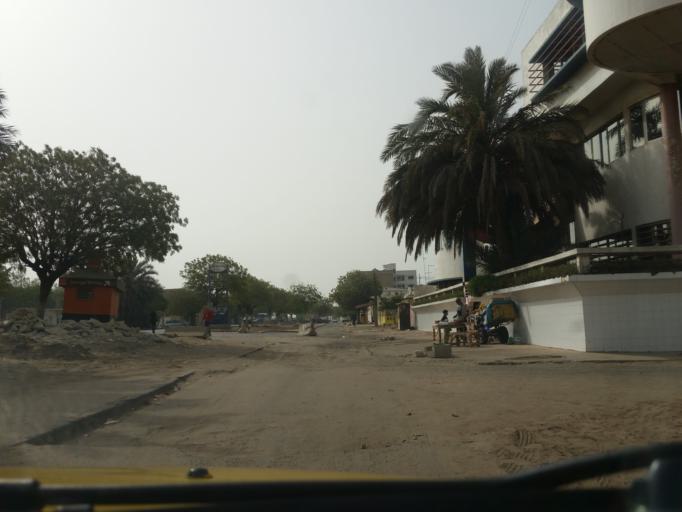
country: SN
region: Dakar
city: Pikine
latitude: 14.7132
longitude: -17.2694
